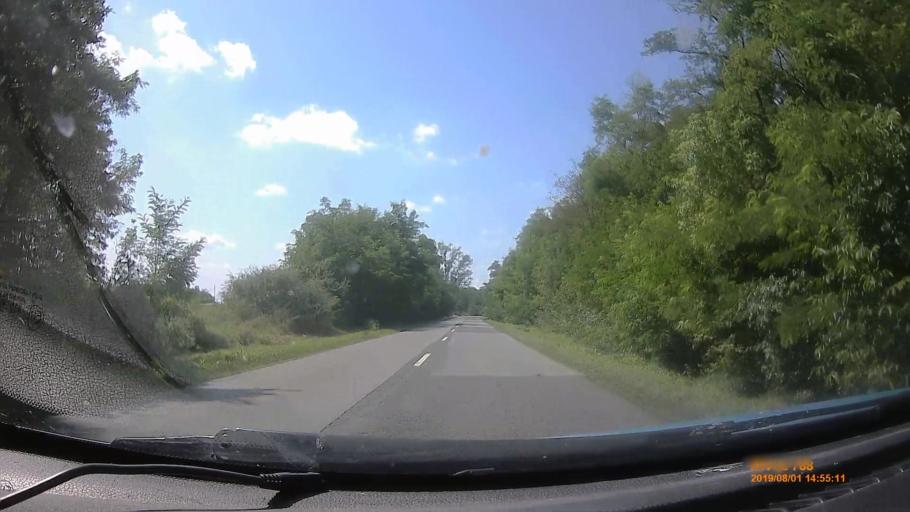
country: HU
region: Baranya
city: Vajszlo
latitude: 45.8689
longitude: 17.9600
